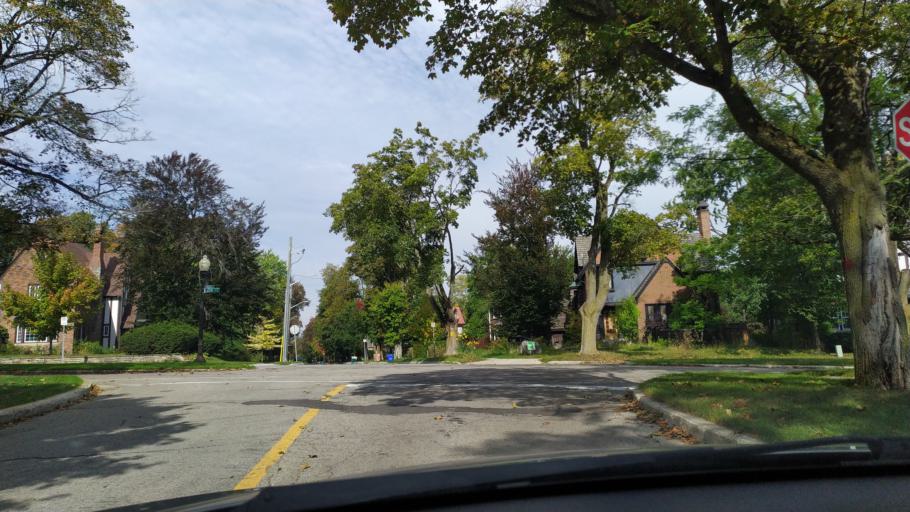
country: CA
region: Ontario
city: Waterloo
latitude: 43.4548
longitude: -80.5237
